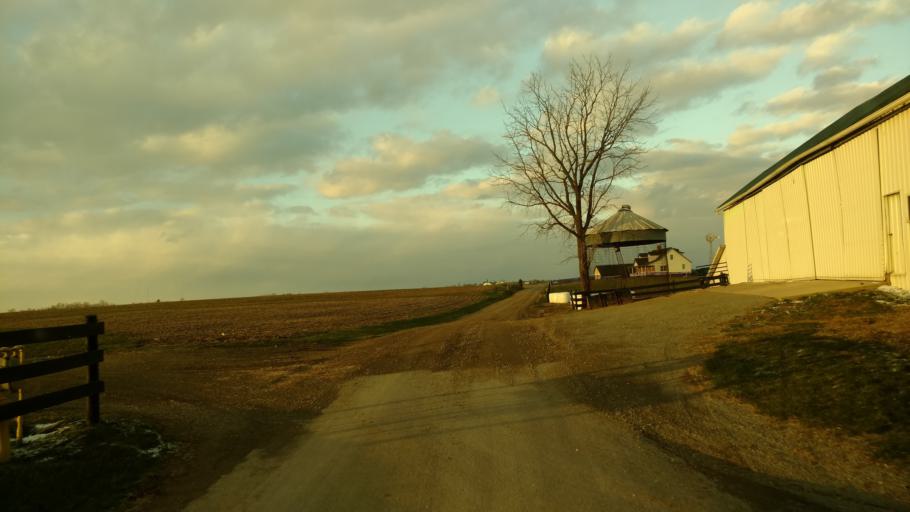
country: US
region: Ohio
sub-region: Tuscarawas County
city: Sugarcreek
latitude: 40.5102
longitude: -81.7701
